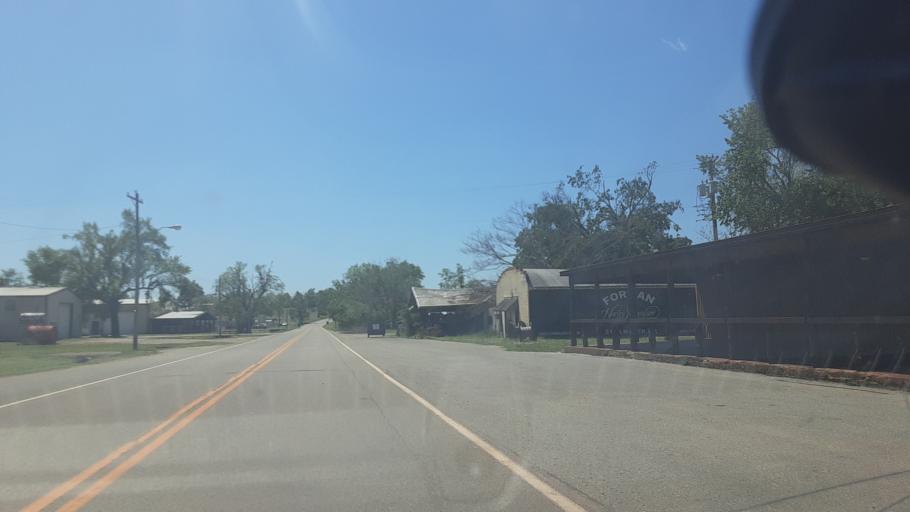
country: US
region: Oklahoma
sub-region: Logan County
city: Guthrie
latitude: 36.0647
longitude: -97.4072
